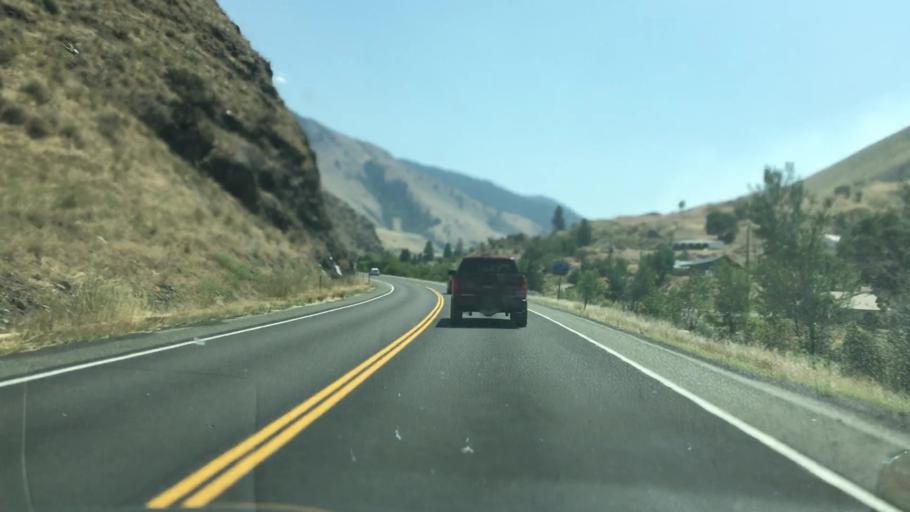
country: US
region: Idaho
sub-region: Valley County
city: McCall
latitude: 45.3572
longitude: -116.3609
